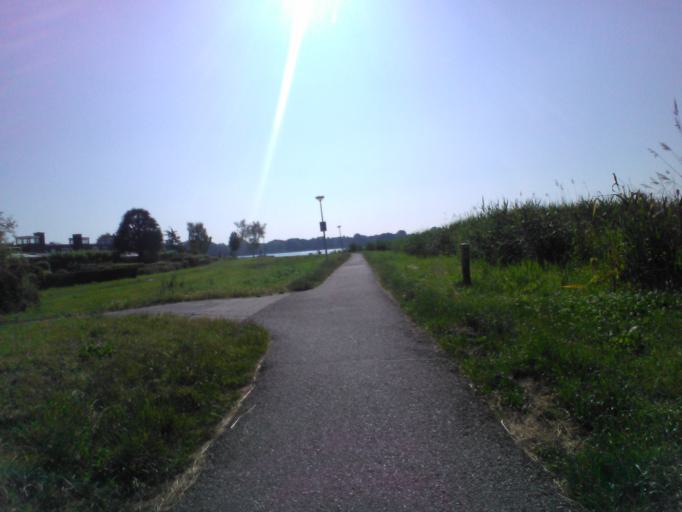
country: NL
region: South Holland
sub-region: Gemeente Alphen aan den Rijn
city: Alphen aan den Rijn
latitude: 52.1384
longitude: 4.6781
